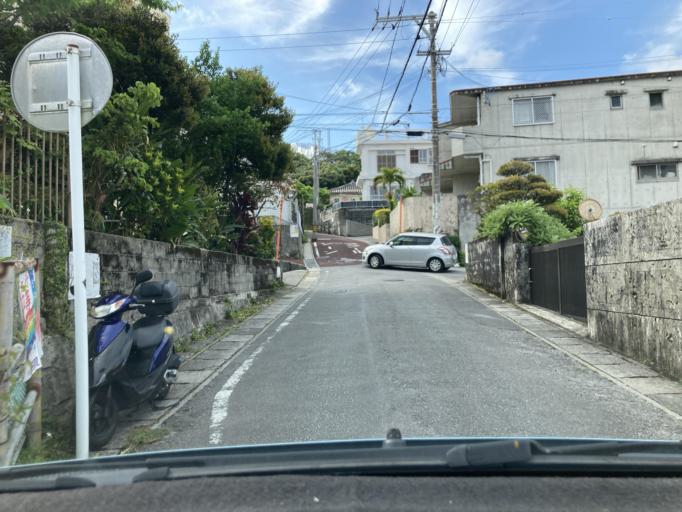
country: JP
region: Okinawa
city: Naha-shi
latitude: 26.2229
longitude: 127.7179
